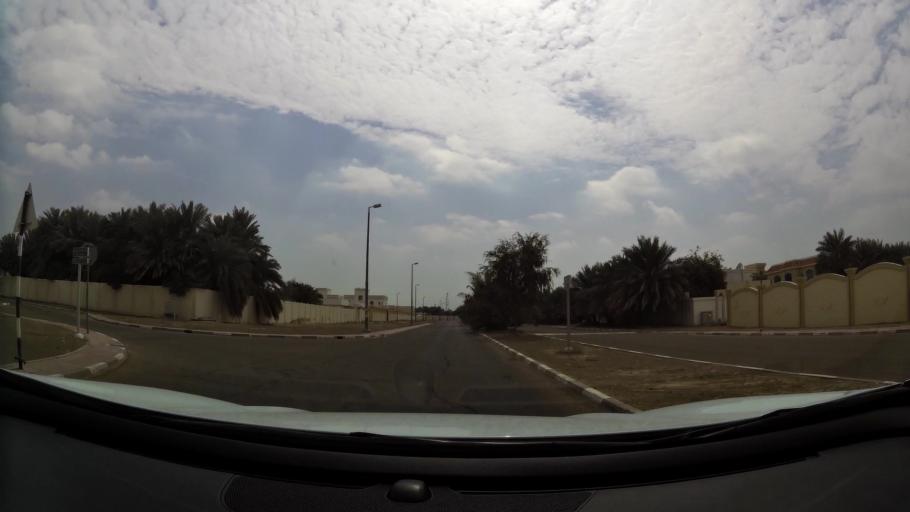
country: AE
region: Abu Dhabi
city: Al Ain
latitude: 24.2026
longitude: 55.7912
